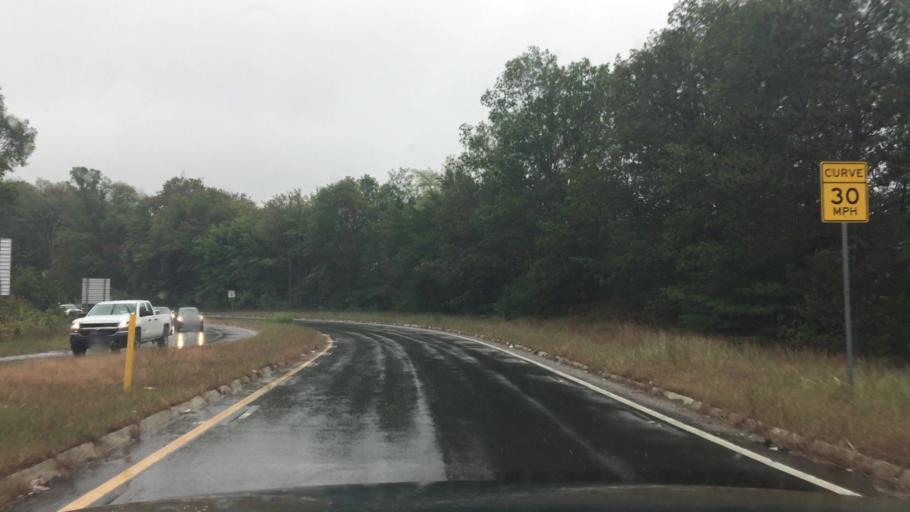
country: US
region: Massachusetts
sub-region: Norfolk County
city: Bellingham
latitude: 42.1137
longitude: -71.4681
